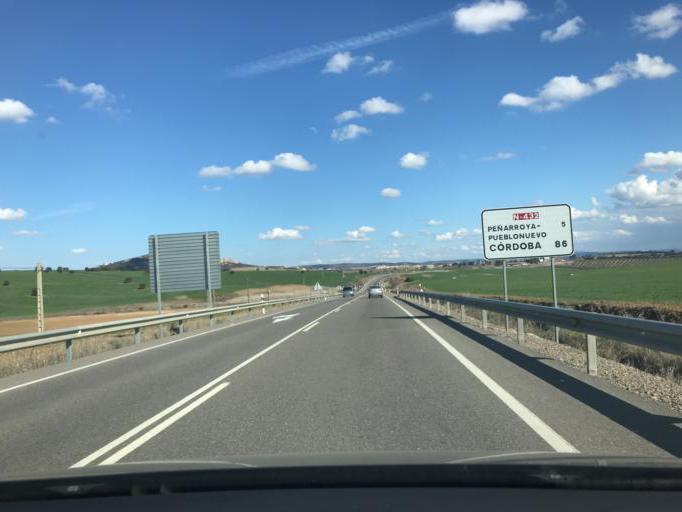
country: ES
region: Andalusia
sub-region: Province of Cordoba
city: Penarroya-Pueblonuevo
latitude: 38.3014
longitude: -5.3324
